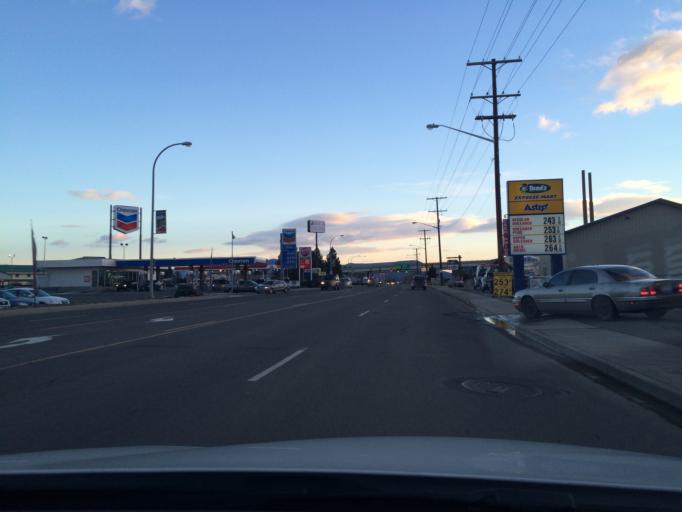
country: US
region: Washington
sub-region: Kittitas County
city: Ellensburg
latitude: 46.9765
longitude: -120.5426
